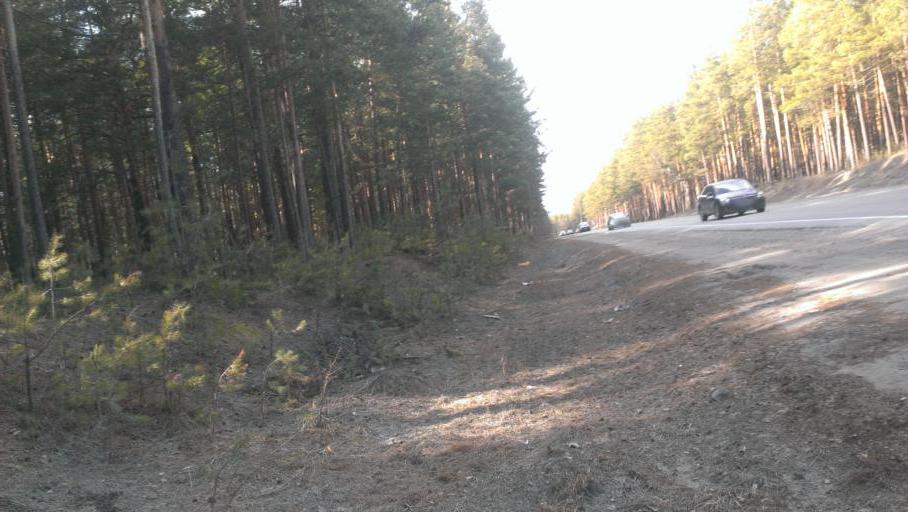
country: RU
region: Altai Krai
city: Yuzhnyy
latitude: 53.2935
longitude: 83.7062
